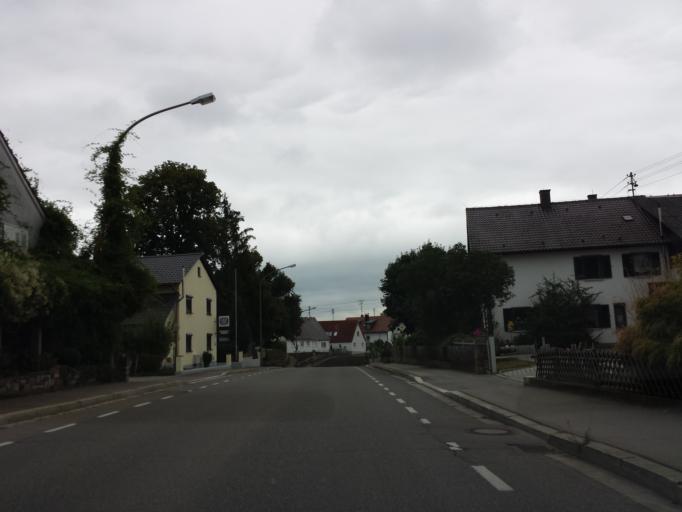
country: DE
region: Bavaria
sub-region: Swabia
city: Guenzburg
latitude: 48.4452
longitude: 10.2826
